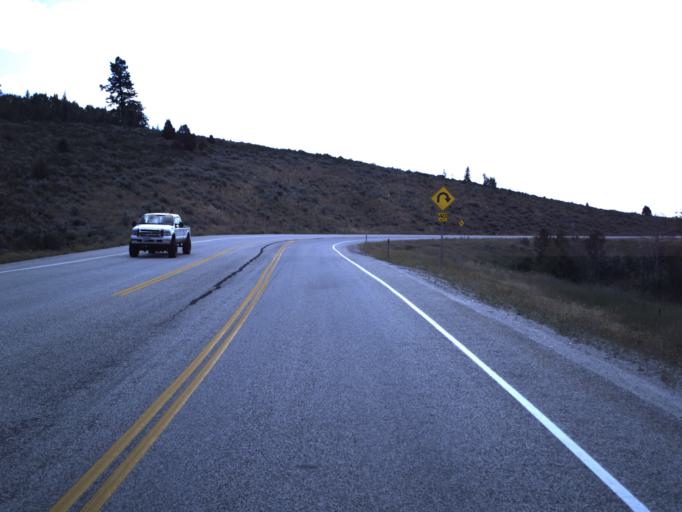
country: US
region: Idaho
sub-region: Bear Lake County
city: Paris
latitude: 41.9244
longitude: -111.4263
